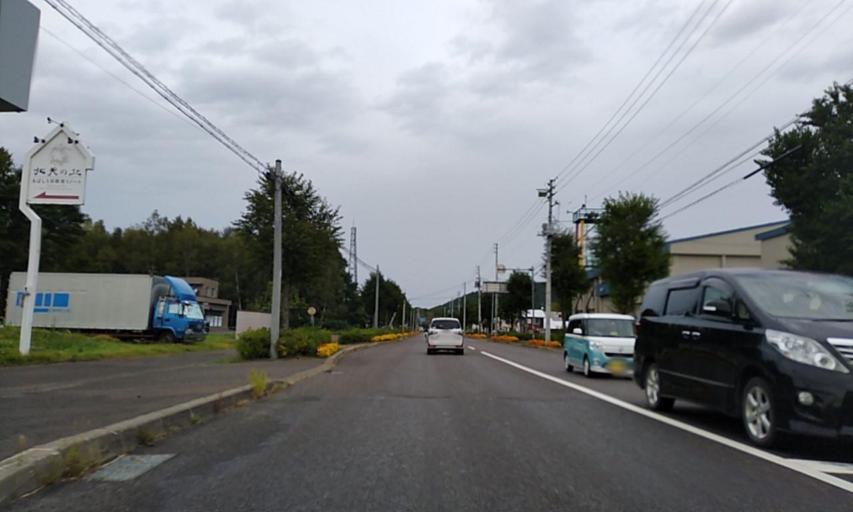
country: JP
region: Hokkaido
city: Abashiri
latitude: 43.9637
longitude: 144.2179
